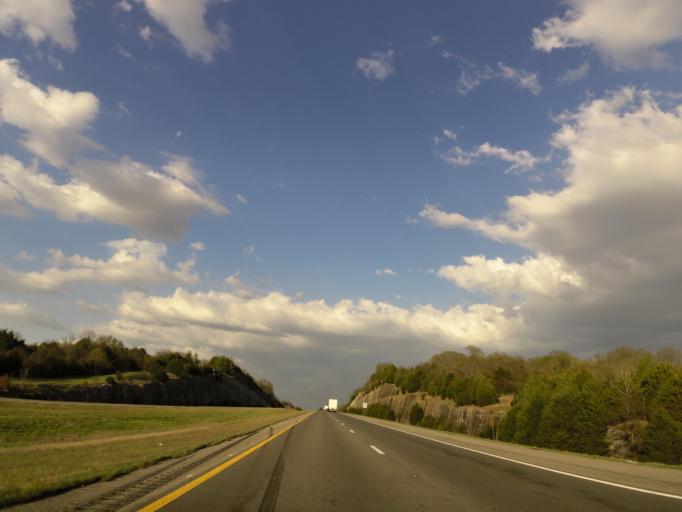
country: US
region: Tennessee
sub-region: Wilson County
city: Rural Hill
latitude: 36.1368
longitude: -86.3860
